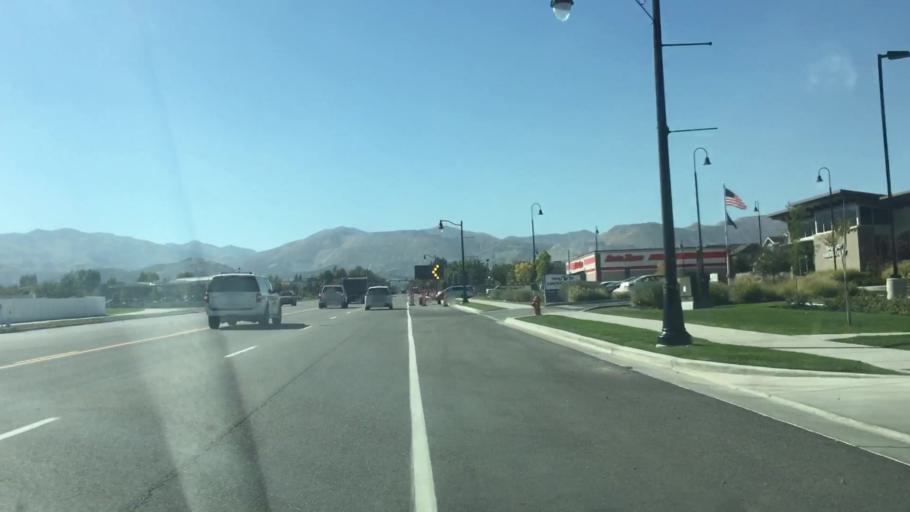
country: US
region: Utah
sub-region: Salt Lake County
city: Herriman
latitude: 40.5080
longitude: -112.0193
